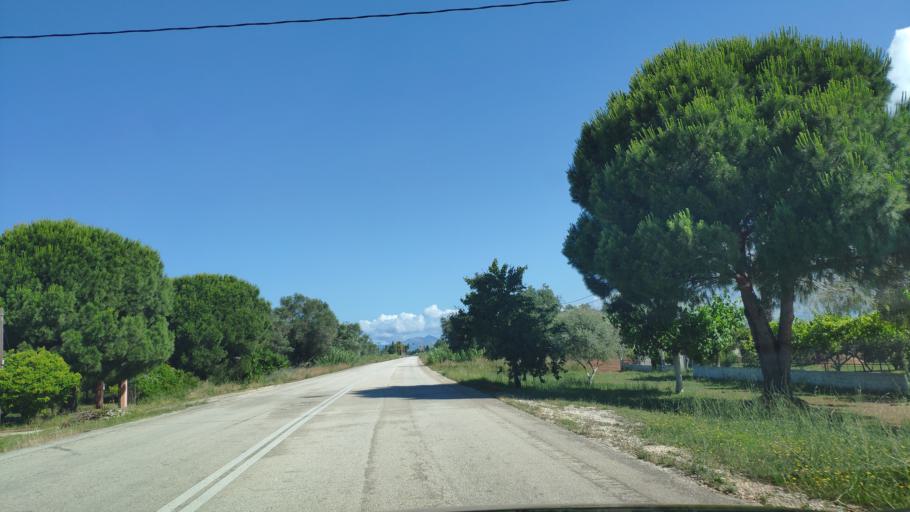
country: GR
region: Epirus
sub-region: Nomos Prevezis
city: Preveza
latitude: 38.9587
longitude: 20.7291
